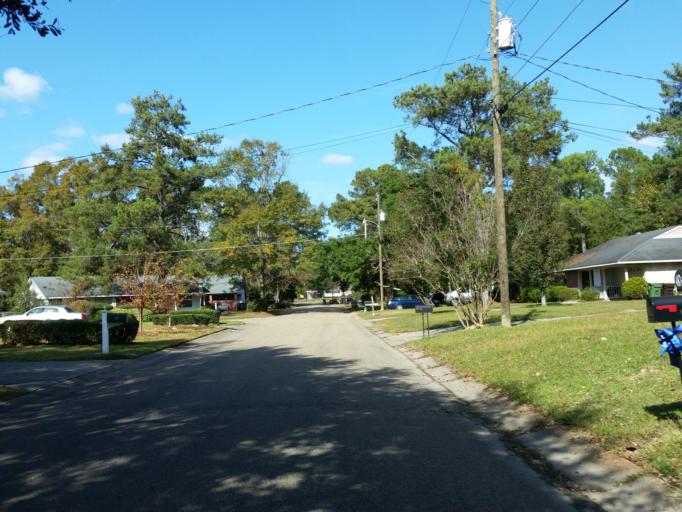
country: US
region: Mississippi
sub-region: Lamar County
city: West Hattiesburg
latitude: 31.3091
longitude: -89.3339
